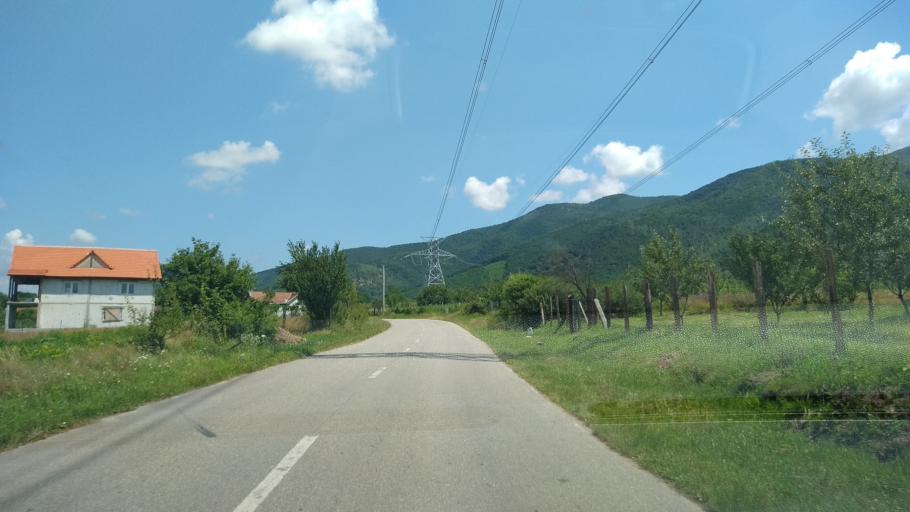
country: RO
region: Hunedoara
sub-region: Comuna Santamaria-Orlea
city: Santamaria-Orlea
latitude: 45.5953
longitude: 23.0075
